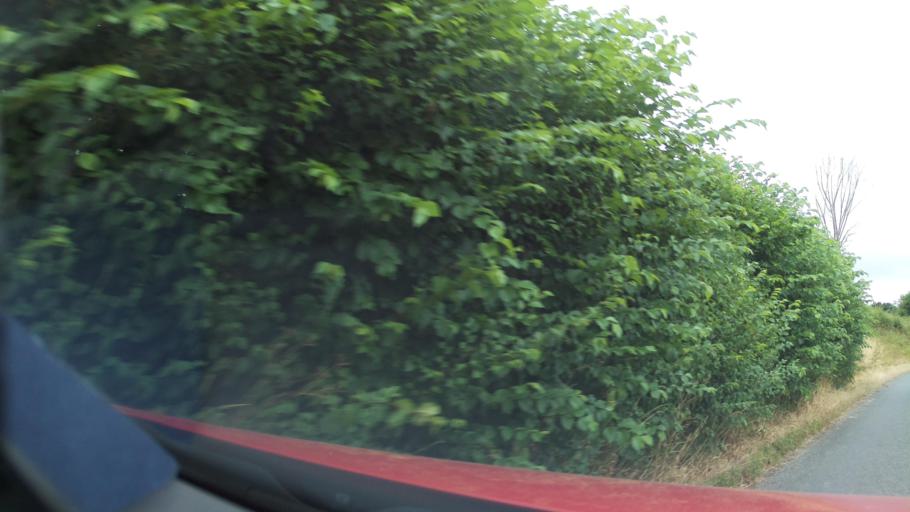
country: GB
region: England
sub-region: Derbyshire
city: Swadlincote
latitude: 52.7909
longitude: -1.5339
